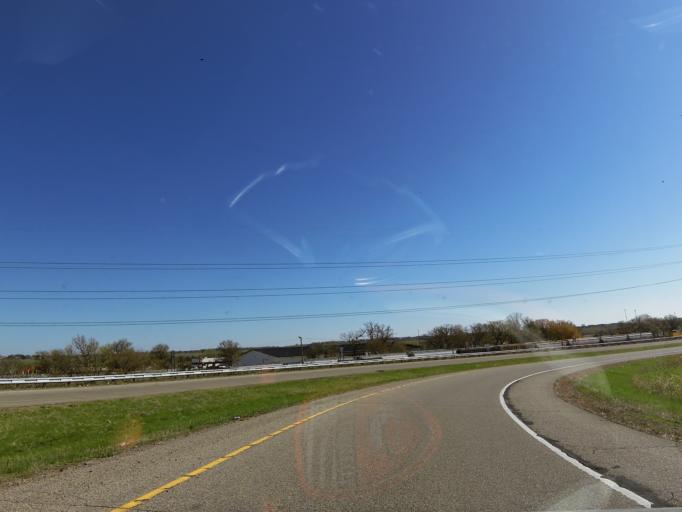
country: US
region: Minnesota
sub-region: Scott County
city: Prior Lake
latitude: 44.7870
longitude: -93.4153
